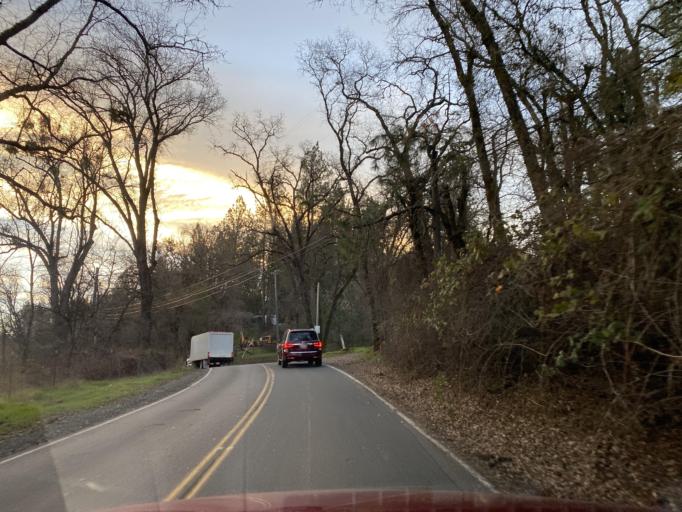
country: US
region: California
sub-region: Amador County
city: Plymouth
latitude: 38.5050
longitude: -120.7644
